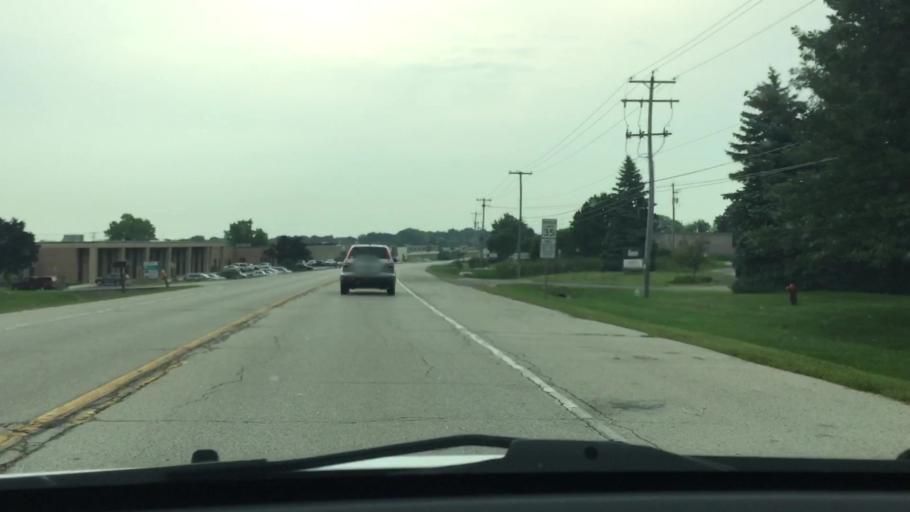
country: US
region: Wisconsin
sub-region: Waukesha County
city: New Berlin
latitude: 42.9949
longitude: -88.1237
